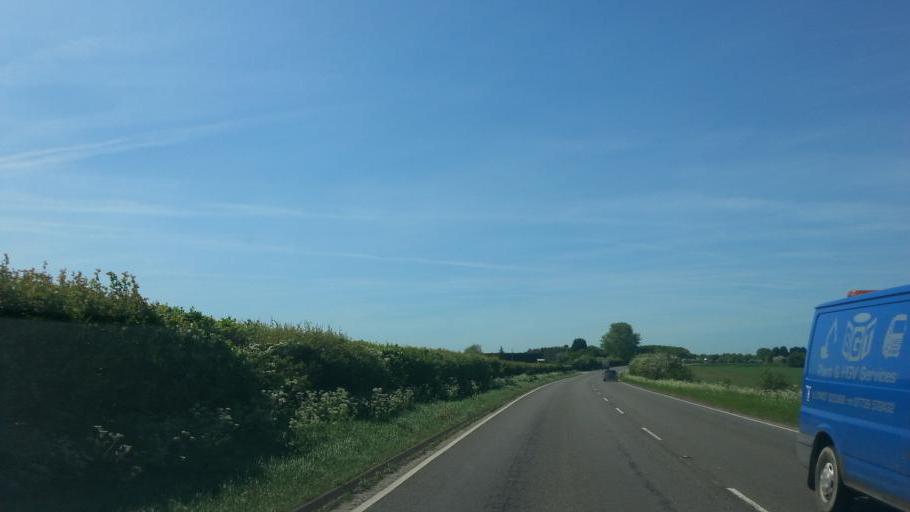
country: GB
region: England
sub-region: Cambridgeshire
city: Warboys
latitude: 52.3947
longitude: -0.0774
